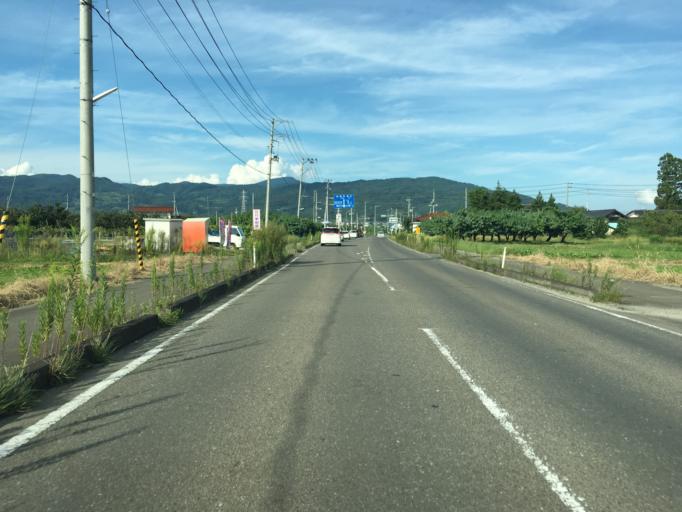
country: JP
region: Fukushima
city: Fukushima-shi
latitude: 37.8127
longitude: 140.4616
